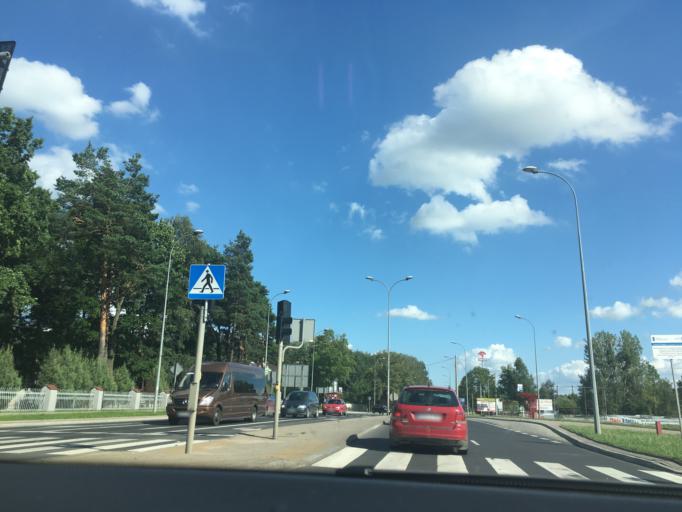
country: PL
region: Podlasie
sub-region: Bialystok
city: Bialystok
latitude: 53.1088
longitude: 23.2107
